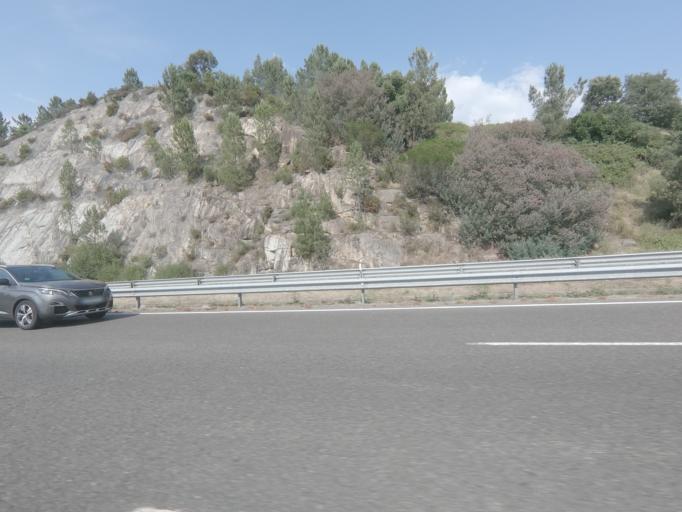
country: ES
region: Galicia
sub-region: Provincia de Ourense
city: Ourense
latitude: 42.2908
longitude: -7.8770
